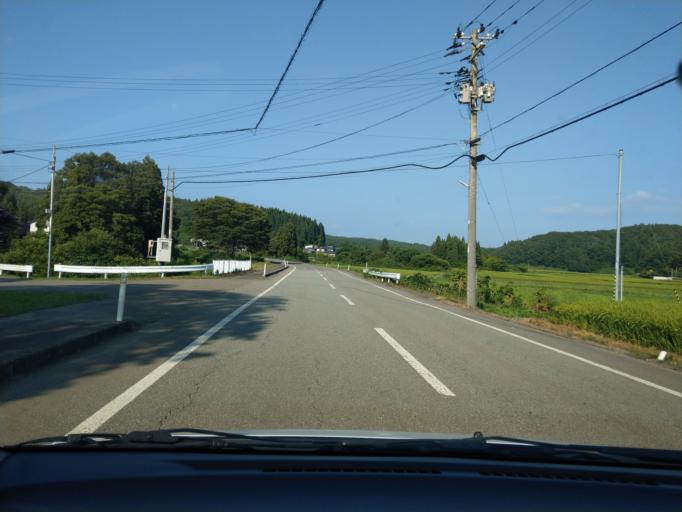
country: JP
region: Akita
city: Akita
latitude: 39.5995
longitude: 140.2143
